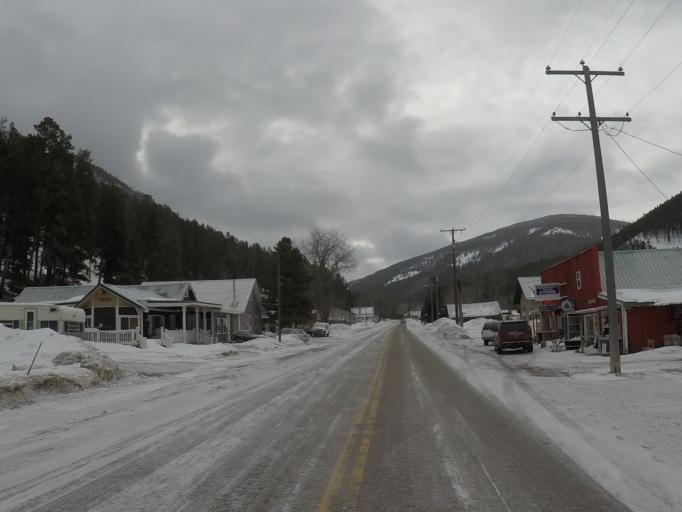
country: US
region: Montana
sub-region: Meagher County
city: White Sulphur Springs
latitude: 46.9331
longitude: -110.7354
